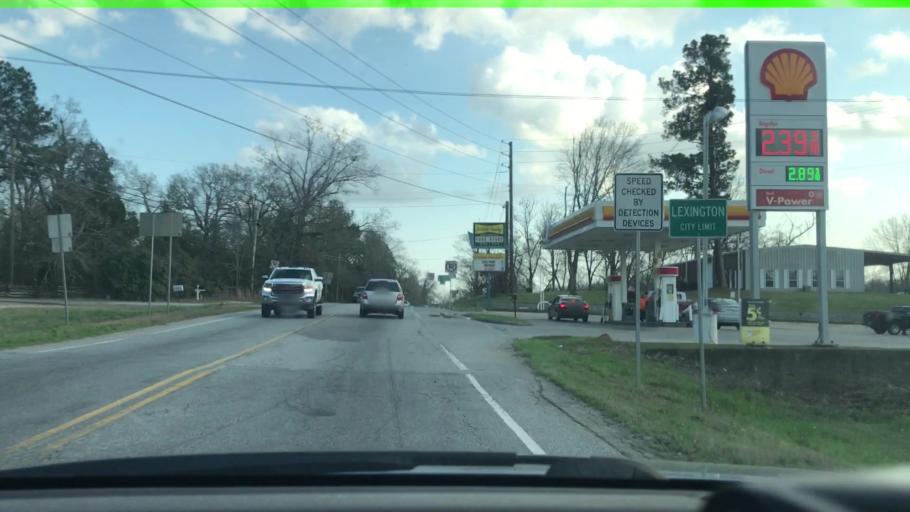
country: US
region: Georgia
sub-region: Oglethorpe County
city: Lexington
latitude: 33.8759
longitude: -83.1165
